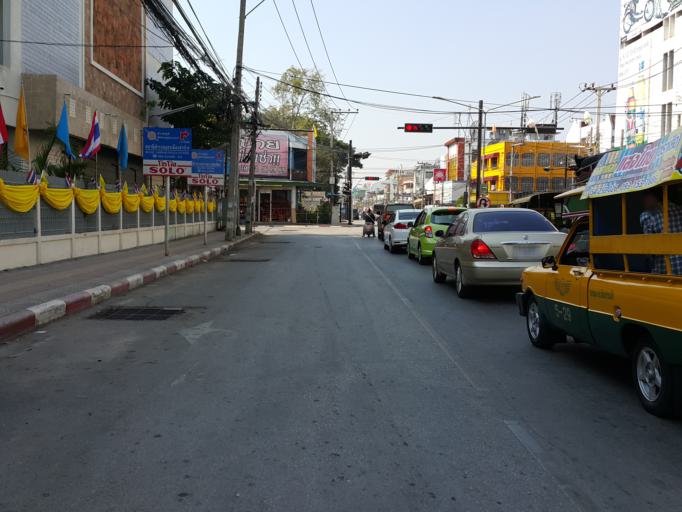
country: TH
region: Lampang
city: Lampang
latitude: 18.2880
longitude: 99.5043
